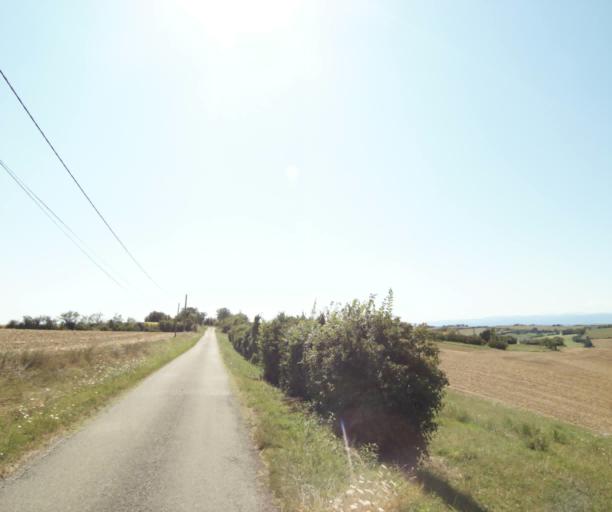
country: FR
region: Midi-Pyrenees
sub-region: Departement de l'Ariege
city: Lezat-sur-Leze
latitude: 43.2582
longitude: 1.3925
